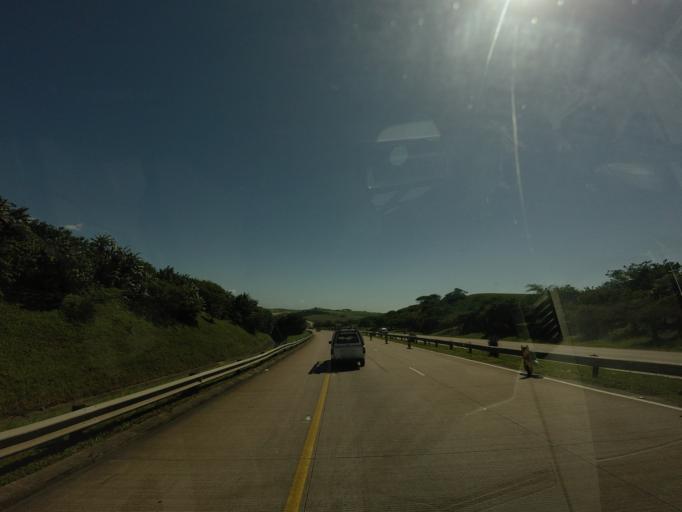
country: ZA
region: KwaZulu-Natal
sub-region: iLembe District Municipality
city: Ballitoville
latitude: -29.4574
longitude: 31.2484
